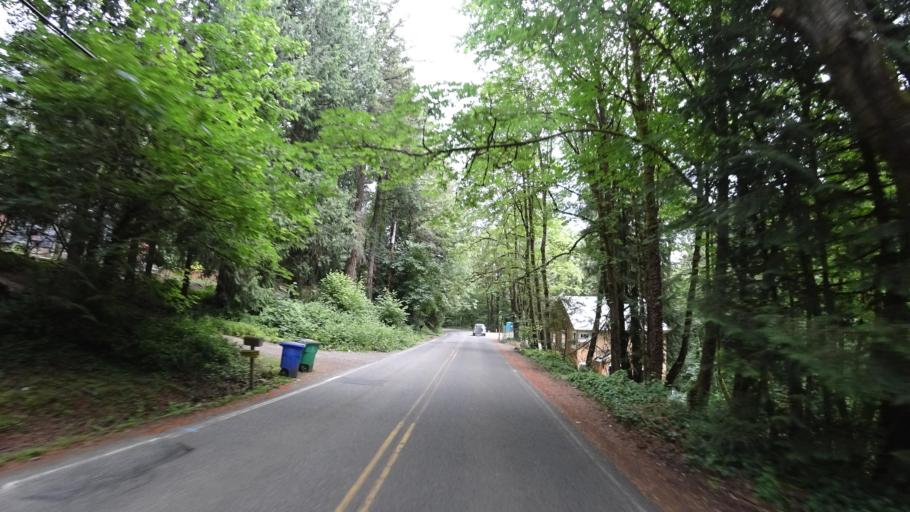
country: US
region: Oregon
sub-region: Clackamas County
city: Lake Oswego
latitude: 45.4560
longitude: -122.7022
